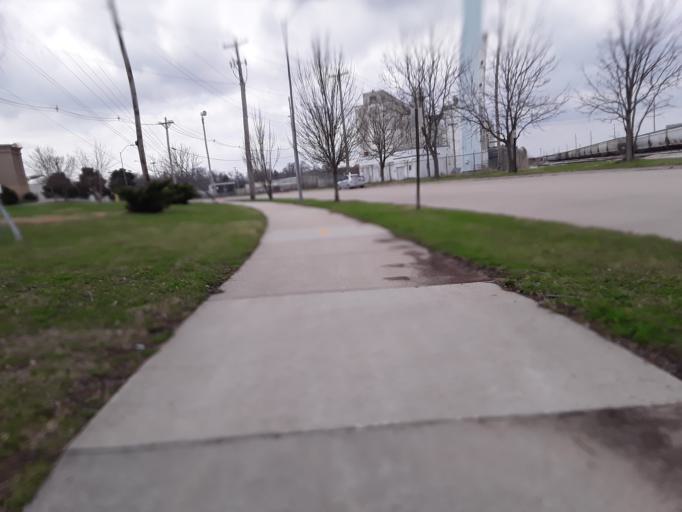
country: US
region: Nebraska
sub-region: Lancaster County
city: Lincoln
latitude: 40.8348
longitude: -96.6827
